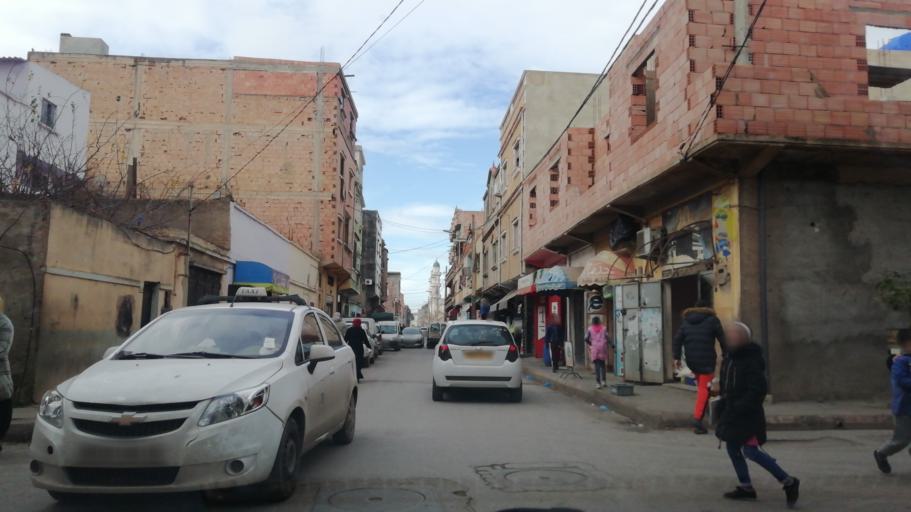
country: DZ
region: Oran
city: Es Senia
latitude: 35.6835
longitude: -0.5978
